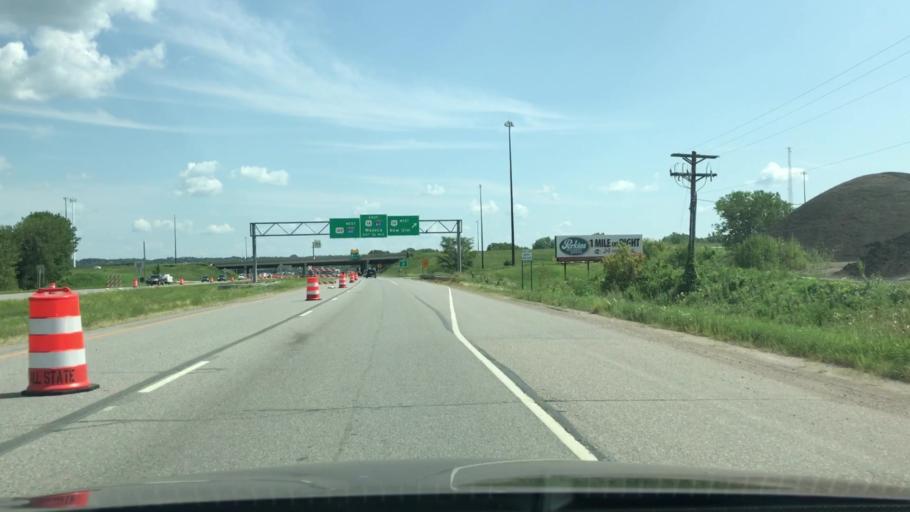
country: US
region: Minnesota
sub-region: Nicollet County
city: North Mankato
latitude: 44.1951
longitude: -94.0195
